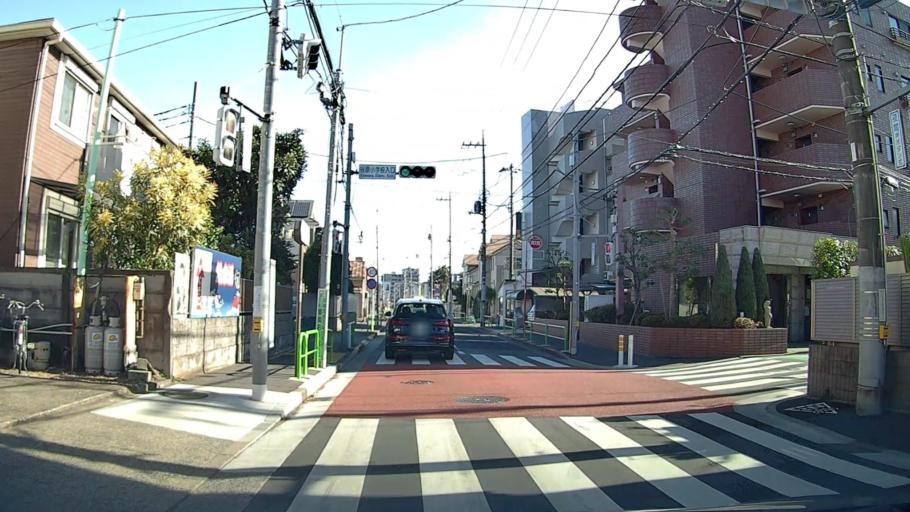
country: JP
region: Saitama
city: Wako
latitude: 35.7524
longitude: 139.6149
